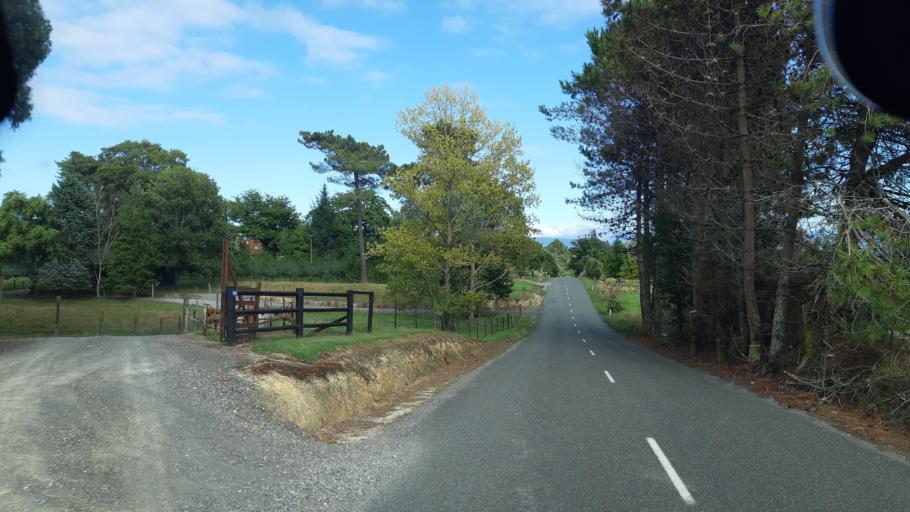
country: NZ
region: Tasman
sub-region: Tasman District
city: Mapua
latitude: -41.2409
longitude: 173.0262
